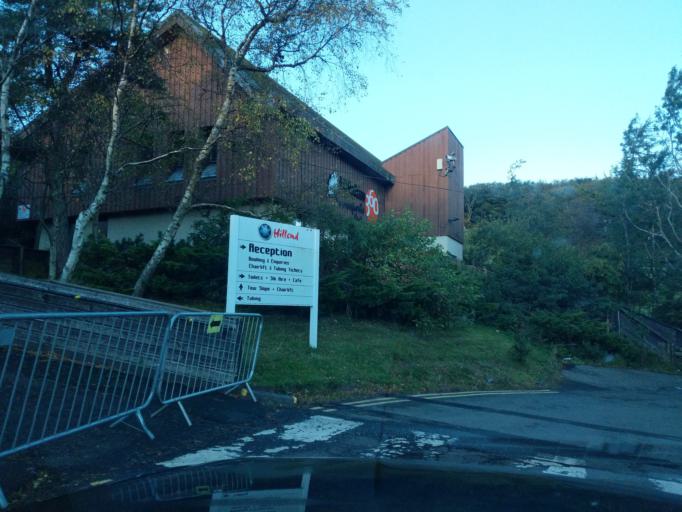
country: GB
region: Scotland
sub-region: Edinburgh
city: Colinton
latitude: 55.8874
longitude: -3.2112
